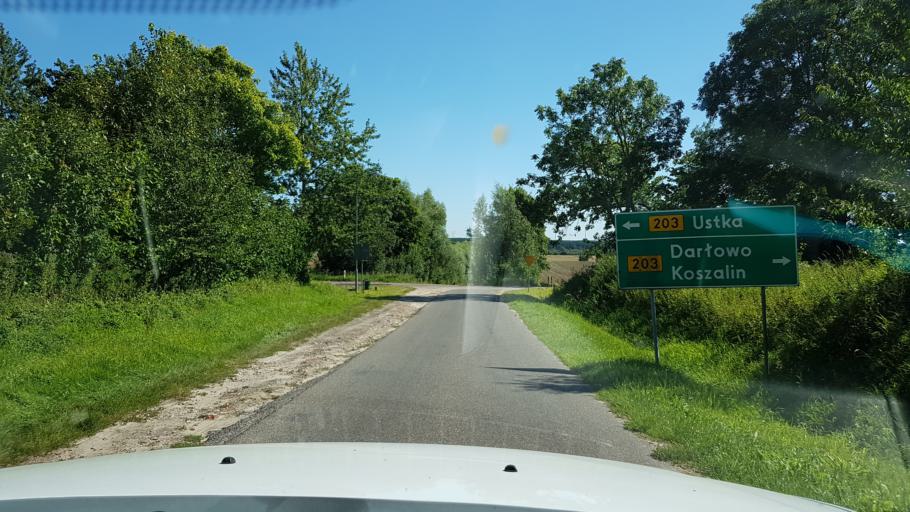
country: PL
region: West Pomeranian Voivodeship
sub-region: Powiat slawienski
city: Darlowo
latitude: 54.4558
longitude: 16.4894
